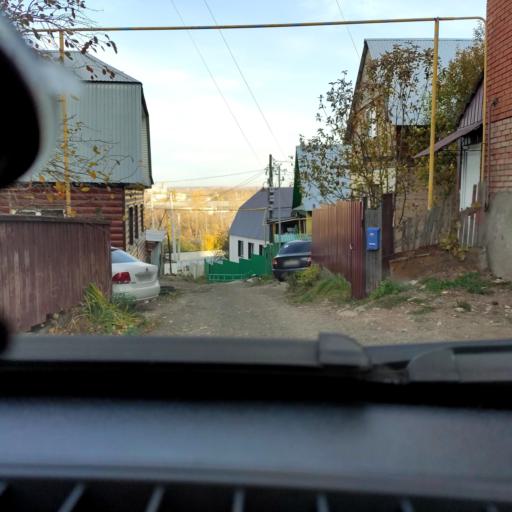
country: RU
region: Bashkortostan
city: Ufa
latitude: 54.7382
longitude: 55.9270
